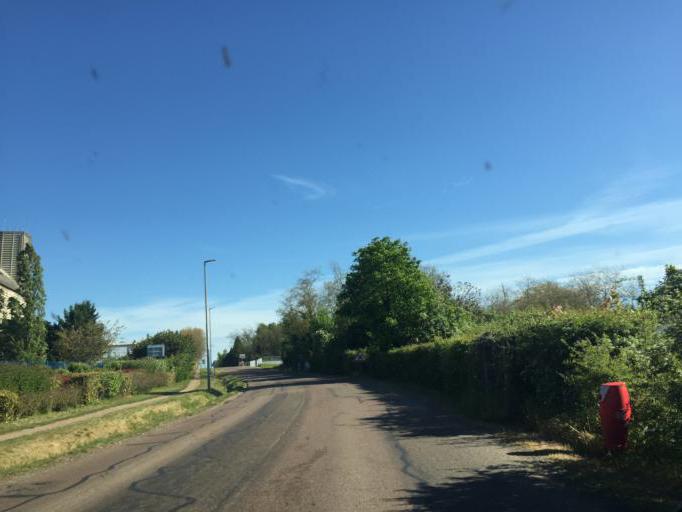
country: FR
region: Bourgogne
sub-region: Departement de la Nievre
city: Clamecy
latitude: 47.4693
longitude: 3.5207
